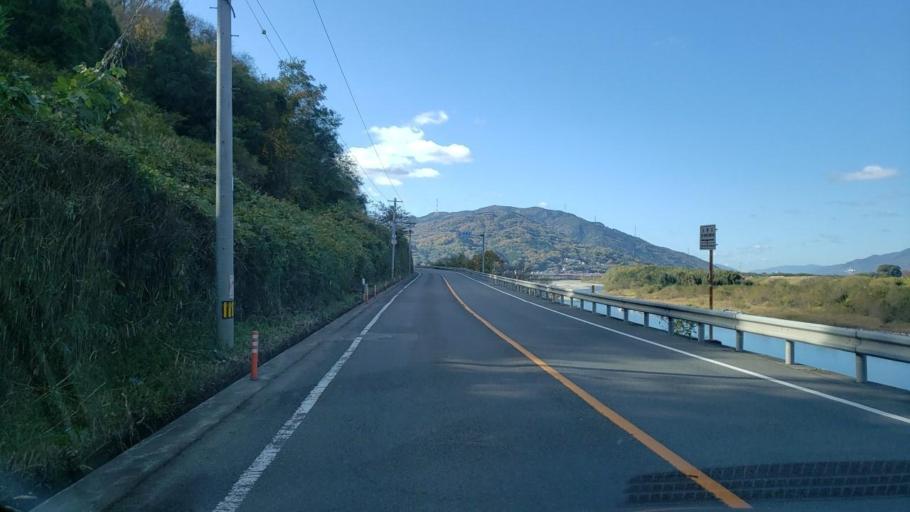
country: JP
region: Tokushima
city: Wakimachi
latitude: 34.0622
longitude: 134.1890
